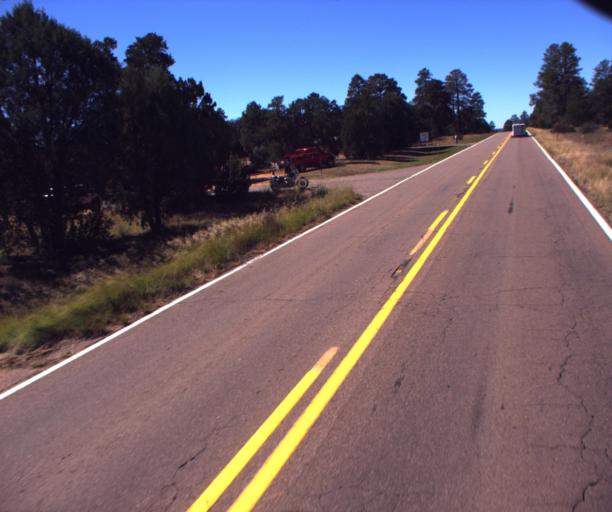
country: US
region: Arizona
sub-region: Navajo County
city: Heber-Overgaard
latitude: 34.4241
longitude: -110.5629
